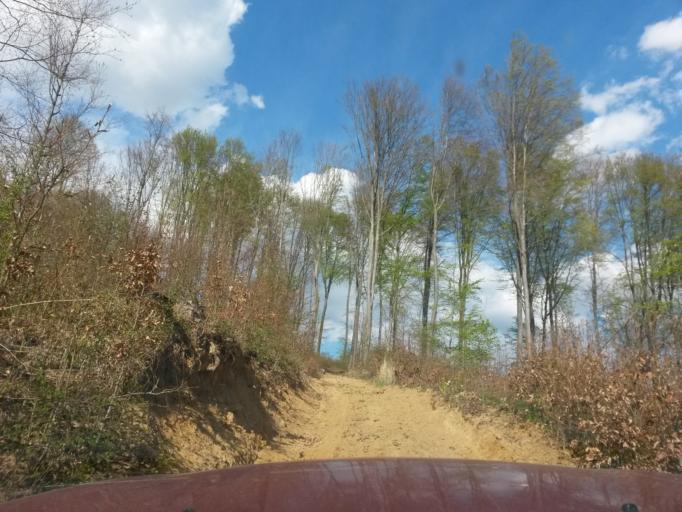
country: SK
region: Presovsky
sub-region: Okres Presov
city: Presov
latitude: 48.9480
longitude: 21.1442
